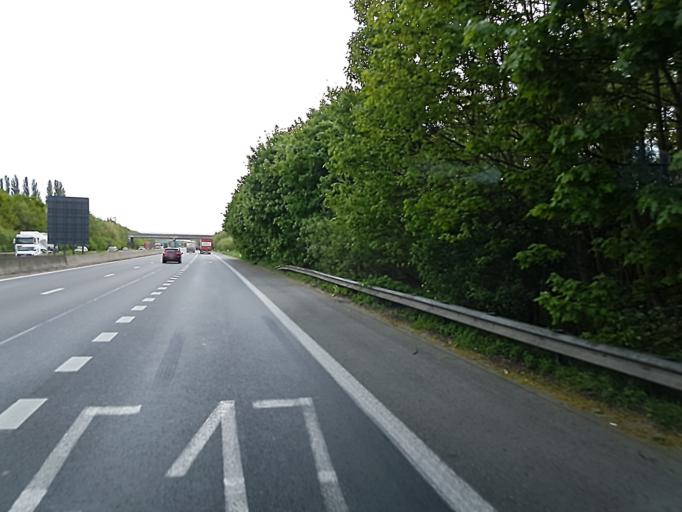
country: BE
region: Flanders
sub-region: Provincie West-Vlaanderen
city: Wevelgem
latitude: 50.8041
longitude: 3.2111
